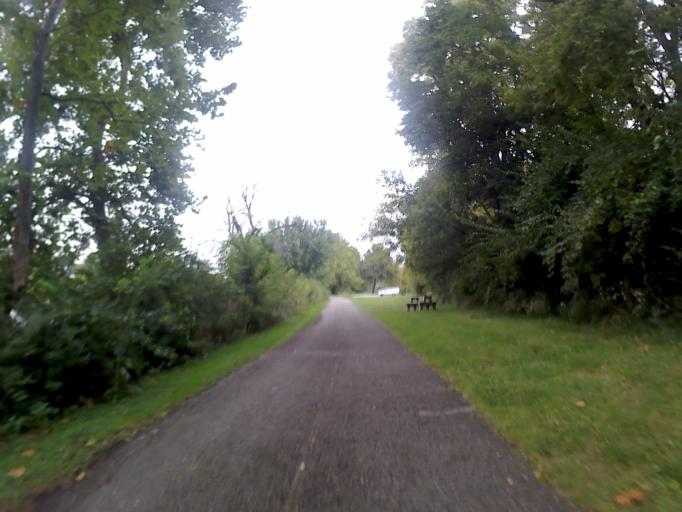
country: US
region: Illinois
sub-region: Kane County
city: Montgomery
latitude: 41.7409
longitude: -88.3285
